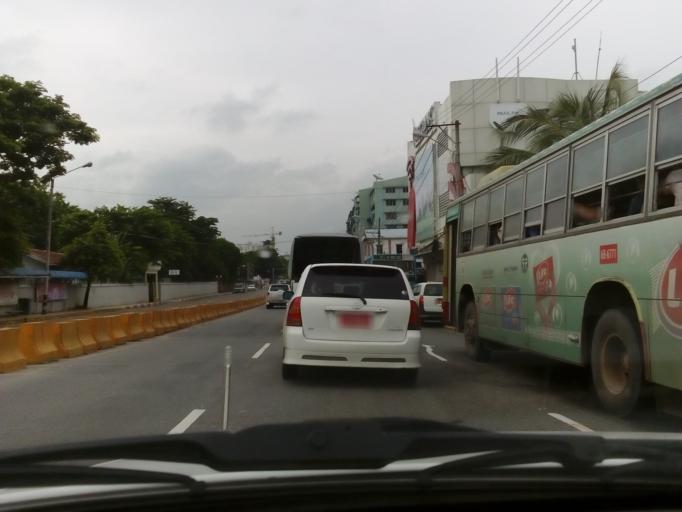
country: MM
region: Yangon
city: Yangon
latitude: 16.8479
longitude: 96.1573
